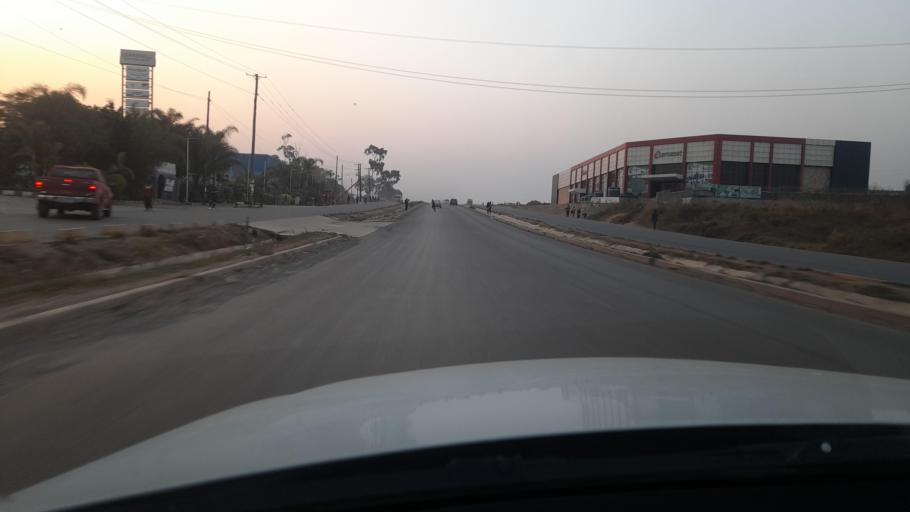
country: ZM
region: Copperbelt
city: Kitwe
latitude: -12.7844
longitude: 28.1980
